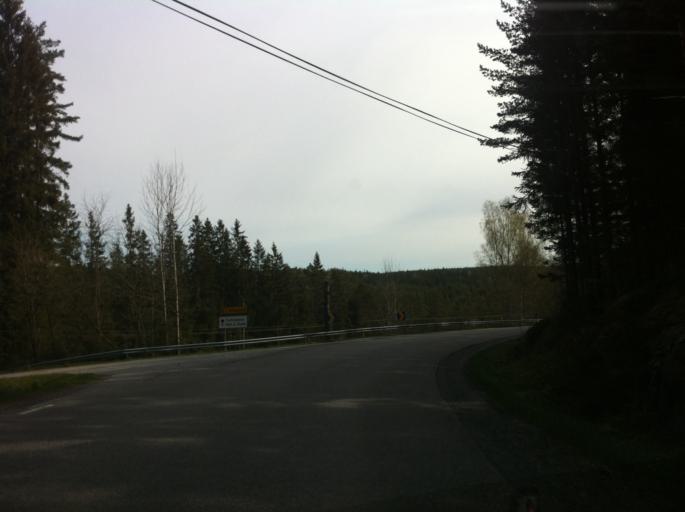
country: SE
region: Vaestra Goetaland
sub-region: Marks Kommun
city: Fritsla
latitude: 57.4000
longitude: 12.8175
